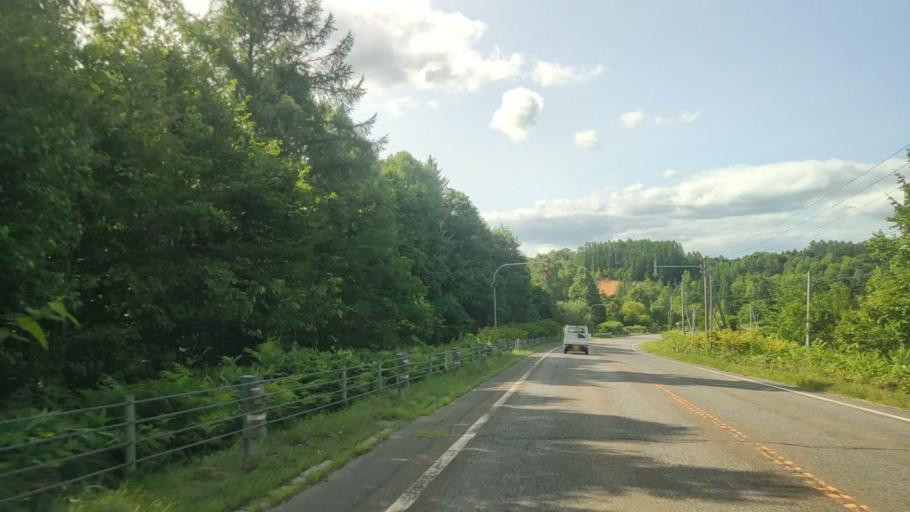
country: JP
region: Hokkaido
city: Nayoro
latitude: 44.3925
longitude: 142.3952
